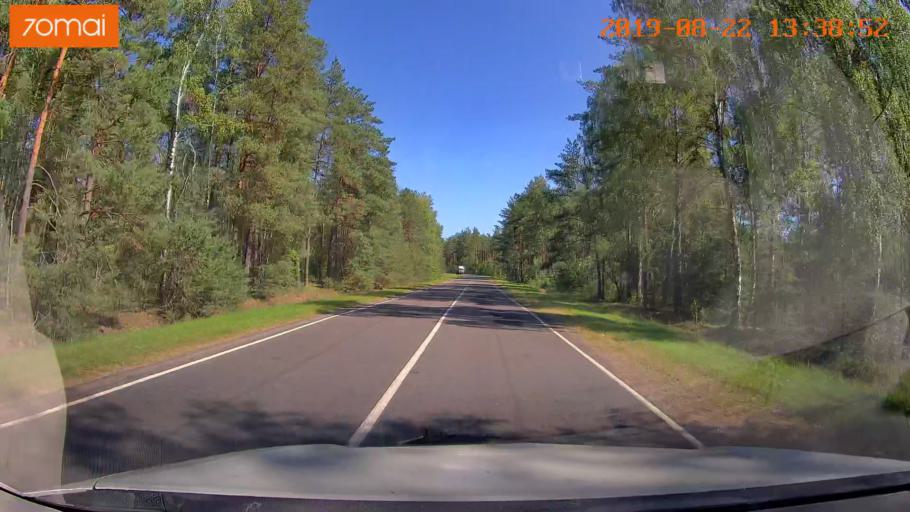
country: BY
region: Minsk
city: Staryya Darohi
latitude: 53.2264
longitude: 28.3351
